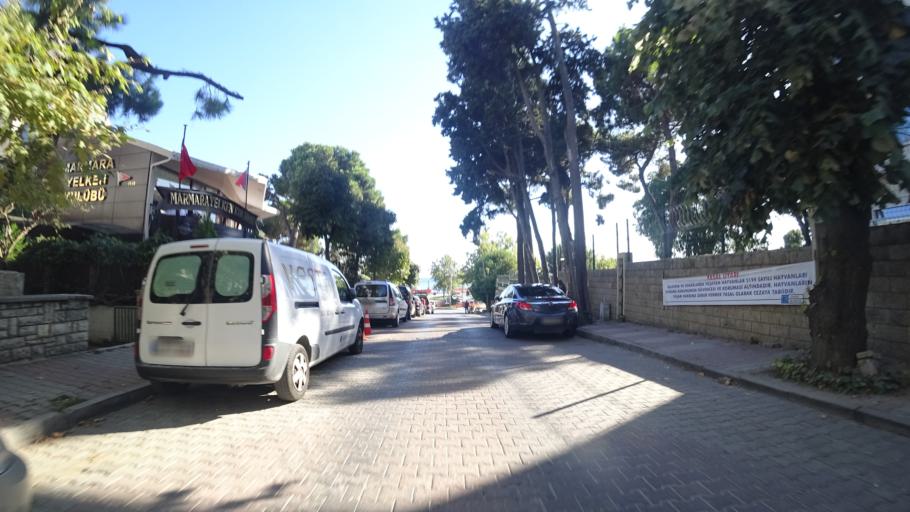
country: TR
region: Istanbul
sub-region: Atasehir
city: Atasehir
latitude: 40.9641
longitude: 29.0687
